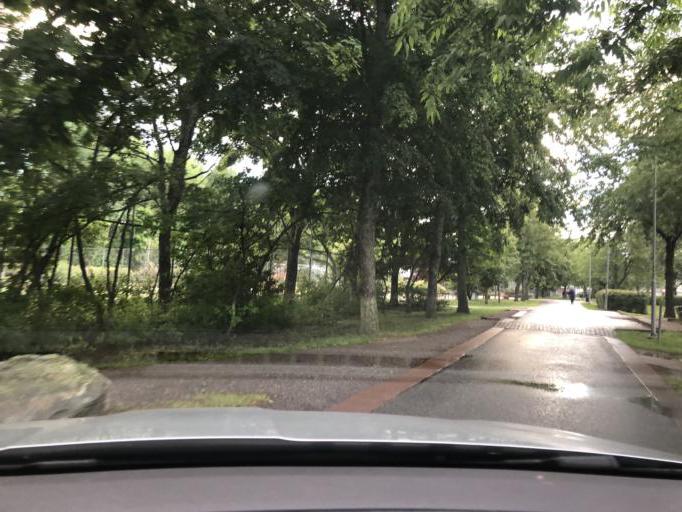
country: SE
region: Stockholm
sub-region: Botkyrka Kommun
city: Alby
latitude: 59.2376
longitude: 17.8479
